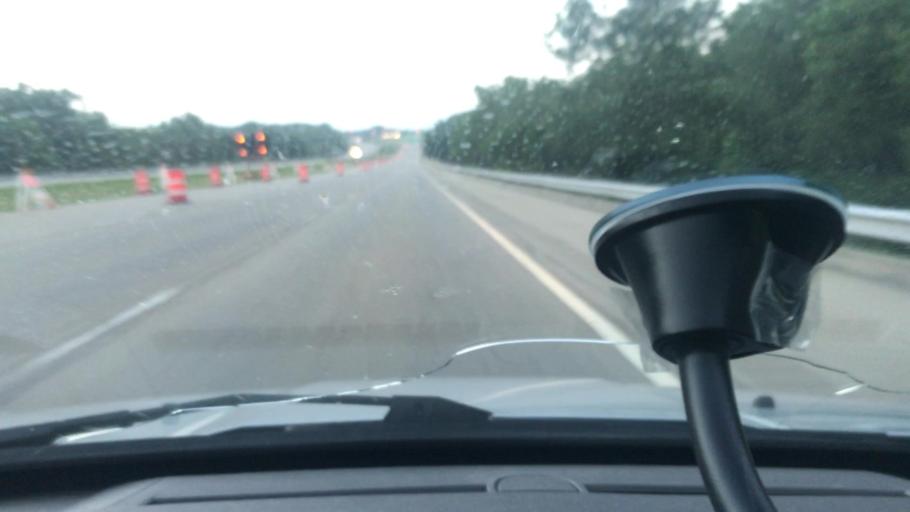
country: US
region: Illinois
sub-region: Peoria County
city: Bellevue
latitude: 40.7275
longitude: -89.6746
